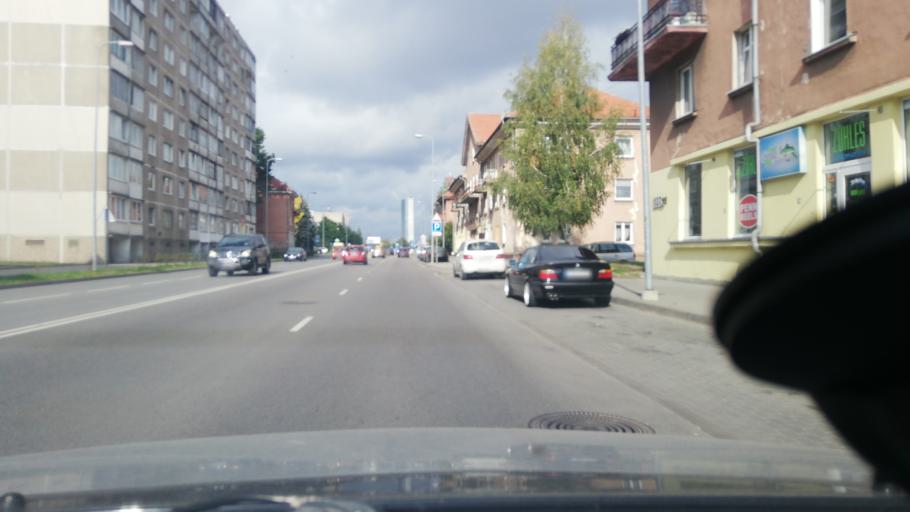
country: LT
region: Klaipedos apskritis
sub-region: Klaipeda
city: Klaipeda
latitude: 55.6793
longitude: 21.1519
